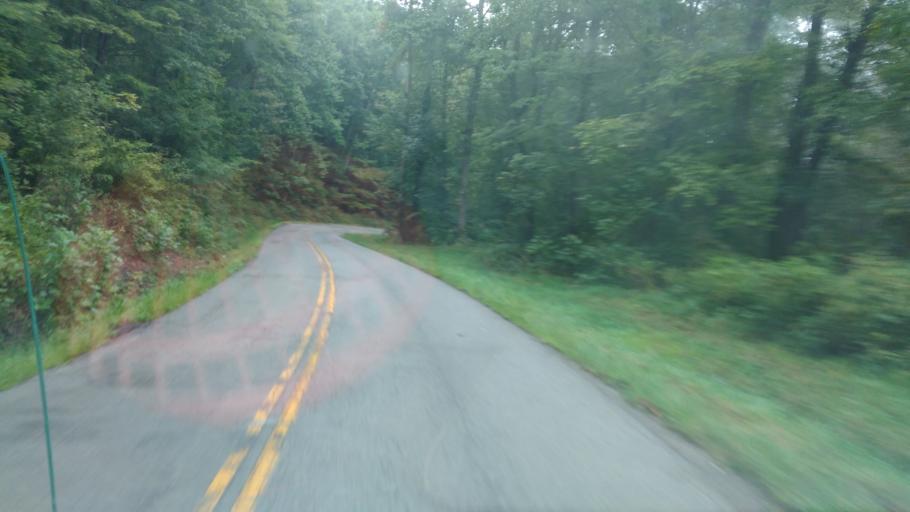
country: US
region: Kentucky
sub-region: Fleming County
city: Flemingsburg
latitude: 38.4106
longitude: -83.5610
